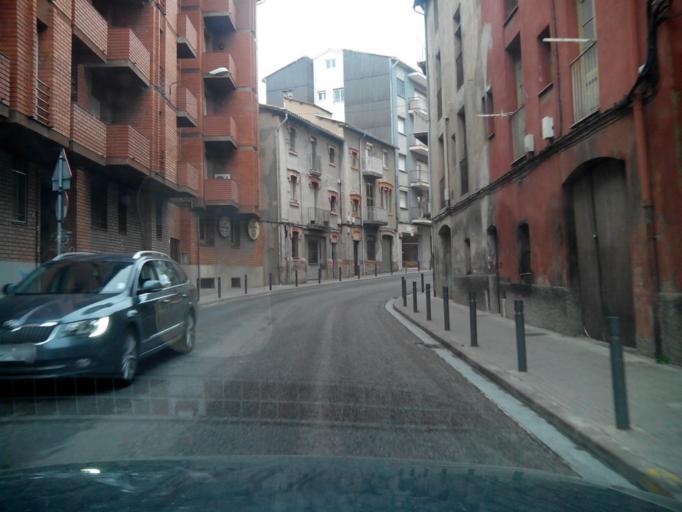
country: ES
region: Catalonia
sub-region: Provincia de Barcelona
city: Berga
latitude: 42.1024
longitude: 1.8462
